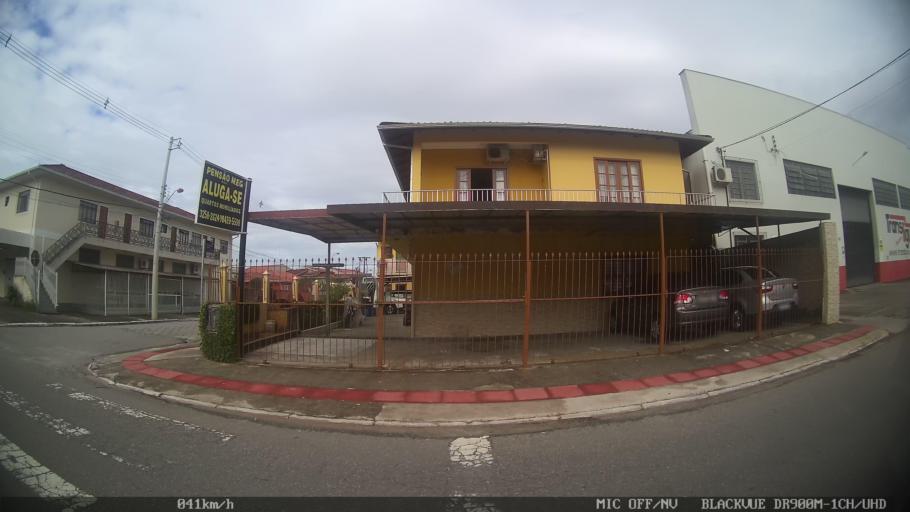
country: BR
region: Santa Catarina
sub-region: Sao Jose
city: Campinas
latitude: -27.5496
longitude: -48.6239
